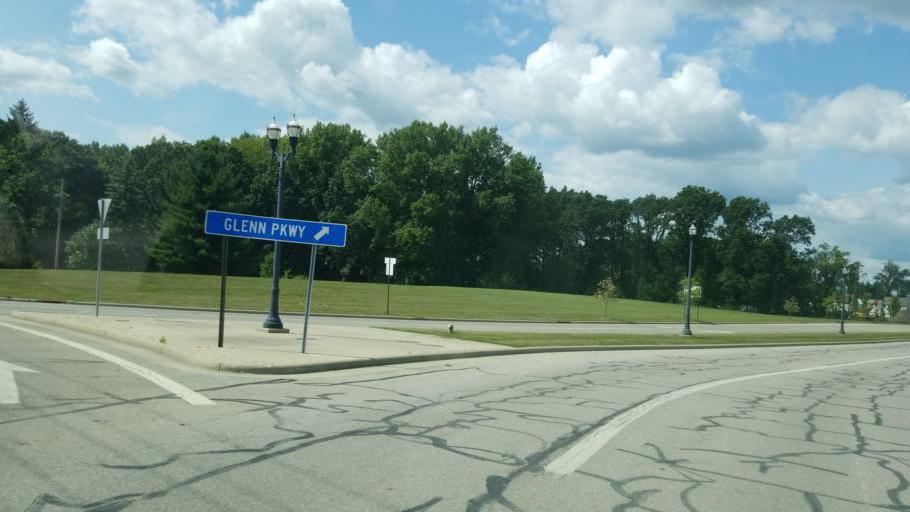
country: US
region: Ohio
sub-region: Delaware County
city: Lewis Center
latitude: 40.2416
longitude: -83.0350
